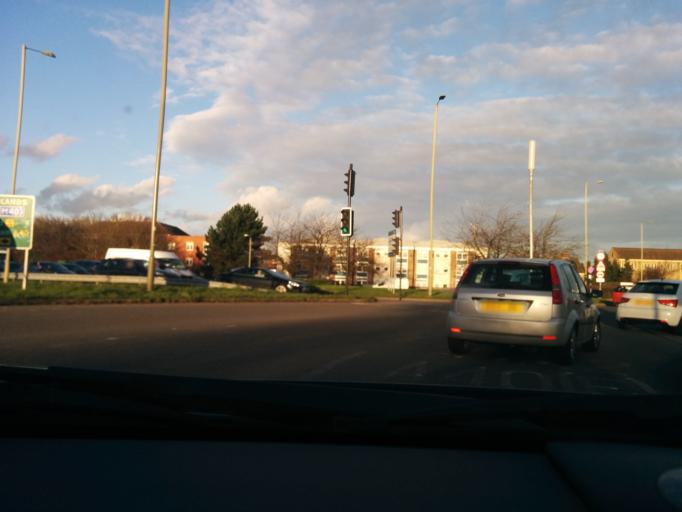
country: GB
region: England
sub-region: Oxfordshire
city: Cowley
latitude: 51.7630
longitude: -1.1972
